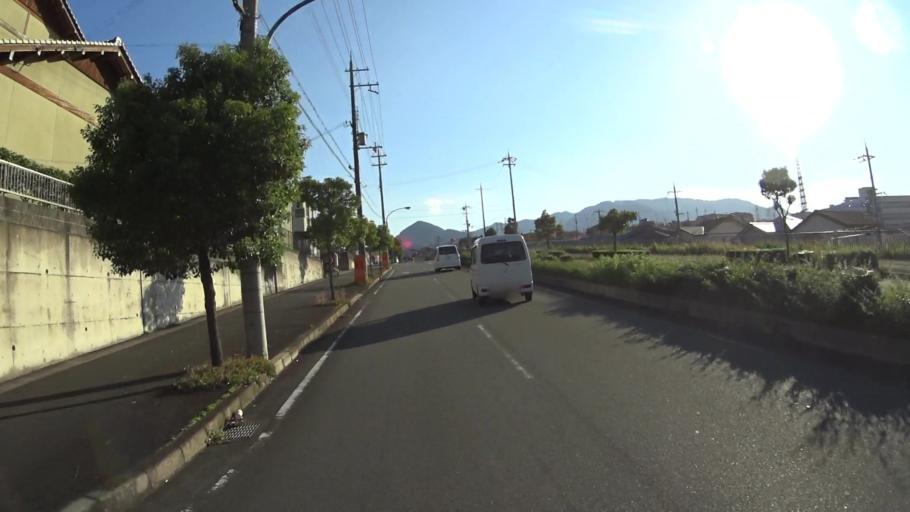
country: JP
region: Kyoto
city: Fukuchiyama
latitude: 35.2921
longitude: 135.1229
